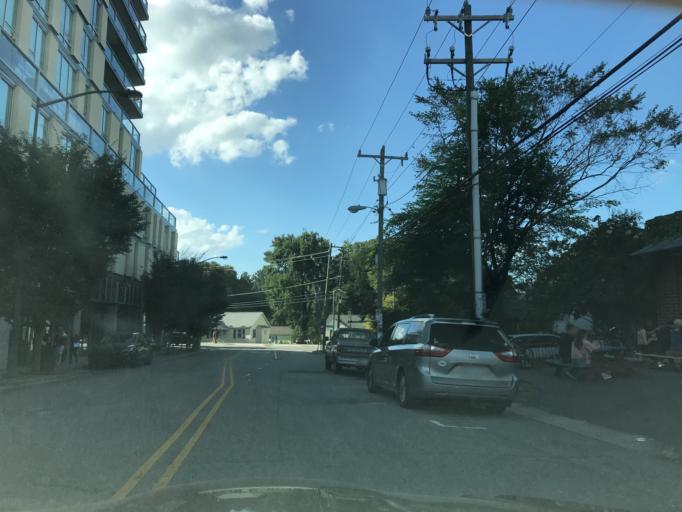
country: US
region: North Carolina
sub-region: Orange County
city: Chapel Hill
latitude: 35.9104
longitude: -79.0646
